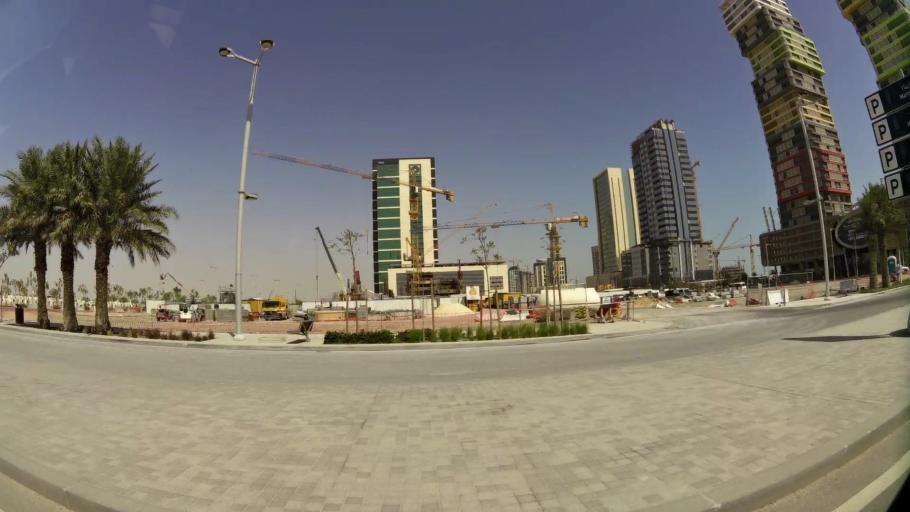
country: QA
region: Baladiyat ad Dawhah
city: Doha
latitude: 25.3859
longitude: 51.5222
